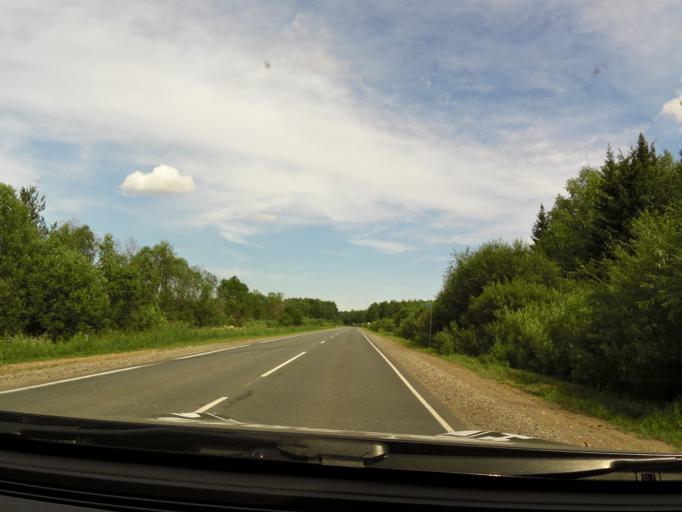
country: RU
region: Kirov
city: Slobodskoy
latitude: 58.7276
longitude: 50.2413
